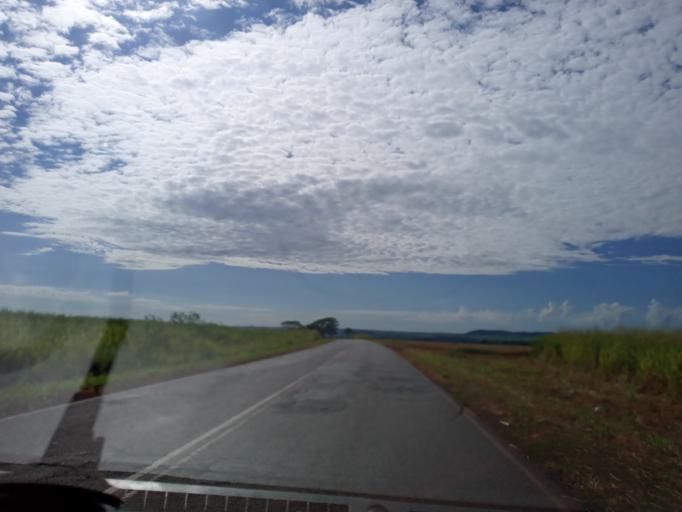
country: BR
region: Goias
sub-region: Itumbiara
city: Itumbiara
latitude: -18.4660
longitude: -49.1261
